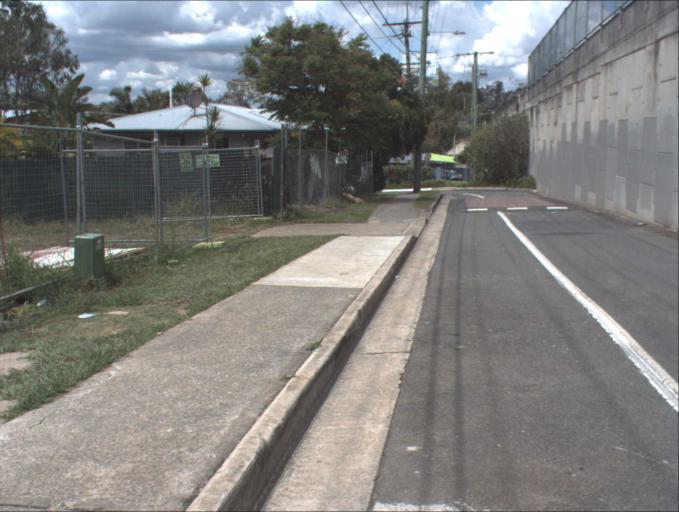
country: AU
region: Queensland
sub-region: Logan
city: Logan City
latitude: -27.6558
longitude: 153.1177
